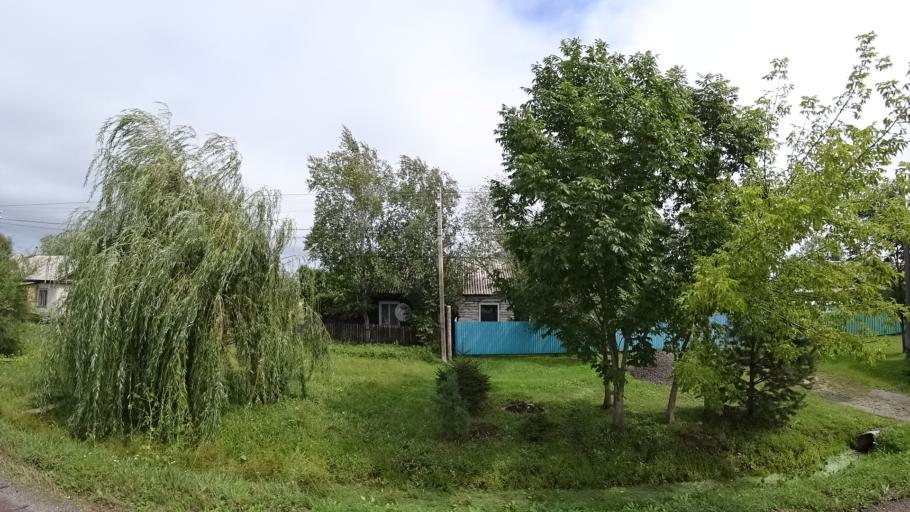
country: RU
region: Primorskiy
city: Monastyrishche
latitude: 44.1977
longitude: 132.4782
